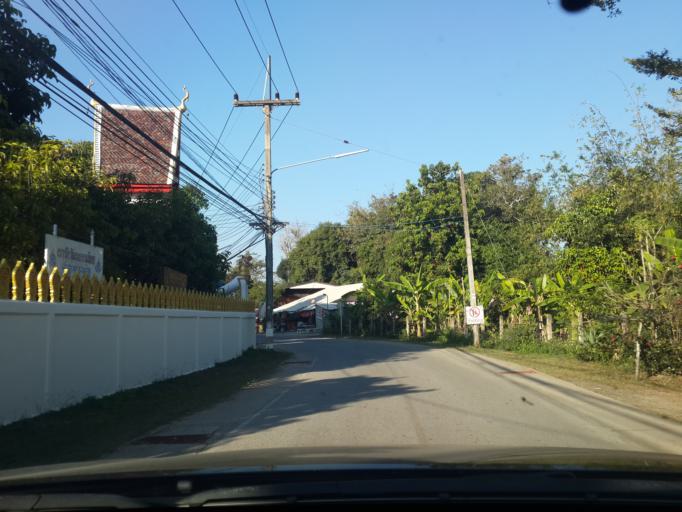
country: TH
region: Chiang Mai
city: San Sai
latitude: 18.9110
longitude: 99.1325
